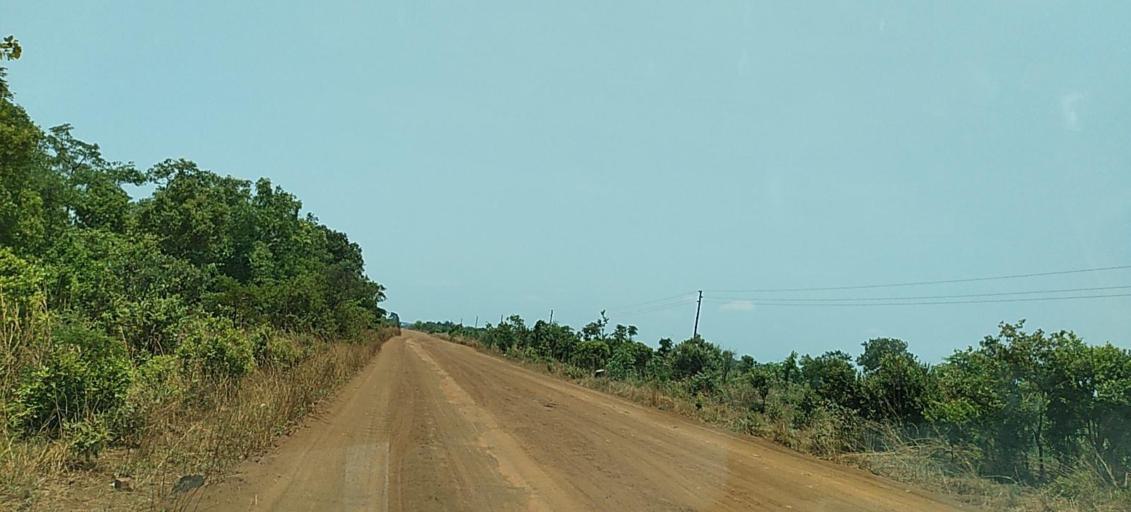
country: ZM
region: Copperbelt
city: Mpongwe
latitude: -13.6839
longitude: 27.8593
